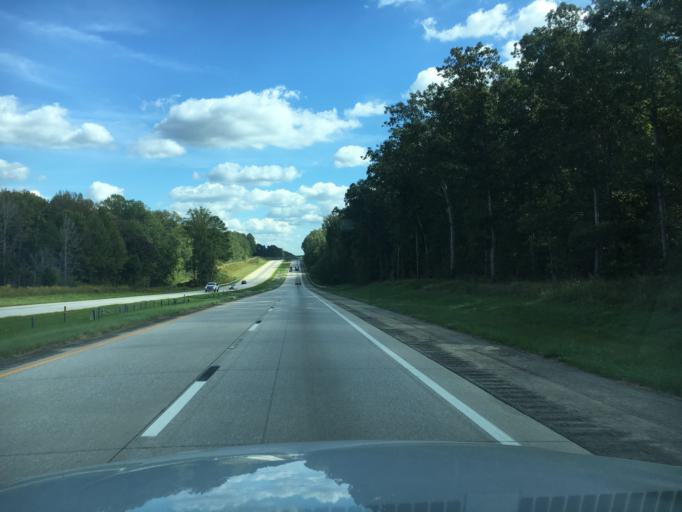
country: US
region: South Carolina
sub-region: Laurens County
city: Watts Mills
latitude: 34.5755
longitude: -82.0364
